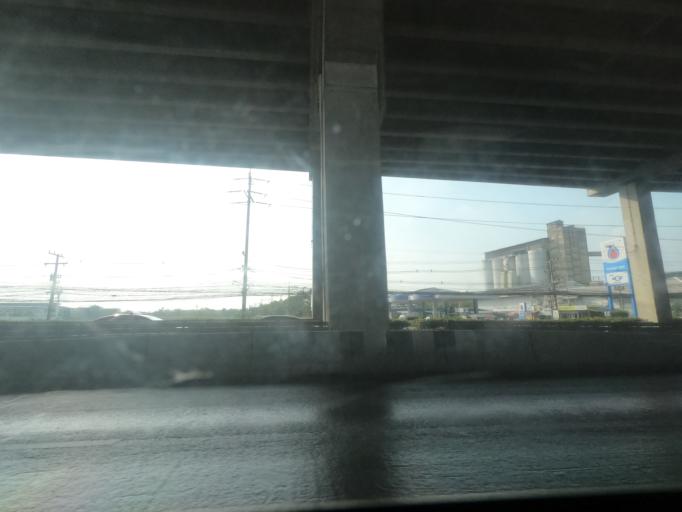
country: TH
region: Phra Nakhon Si Ayutthaya
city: Ban Bang Kadi Pathum Thani
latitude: 13.9972
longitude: 100.6171
